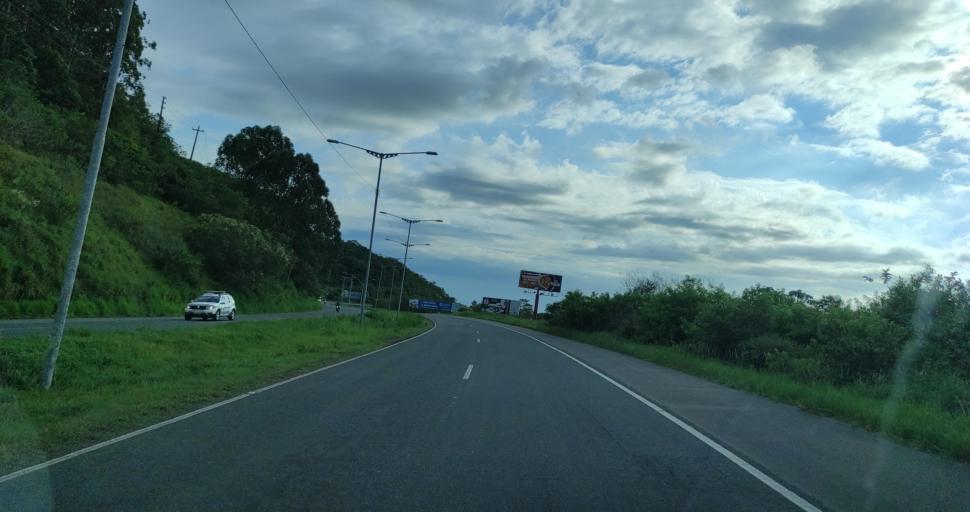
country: BR
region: Santa Catarina
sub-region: Penha
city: Penha
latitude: -26.8078
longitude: -48.6495
